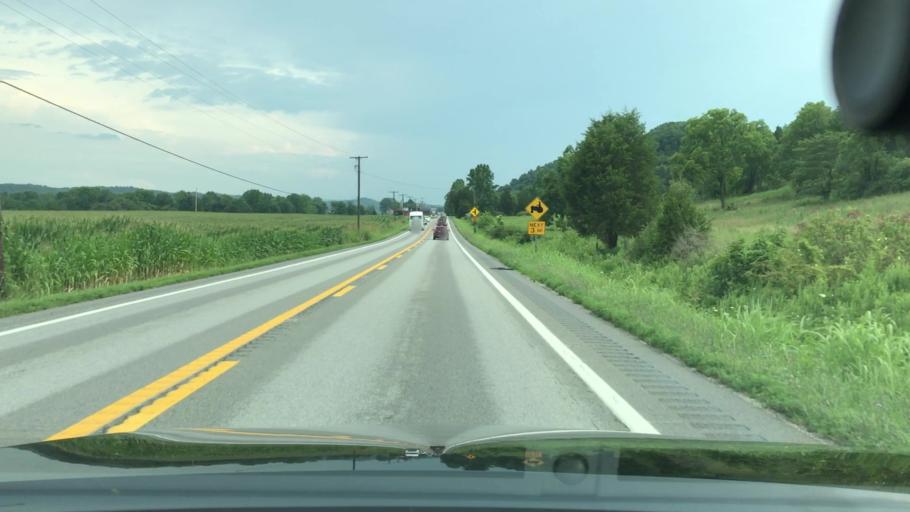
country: US
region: West Virginia
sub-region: Putnam County
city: Buffalo
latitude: 38.7259
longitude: -81.9717
